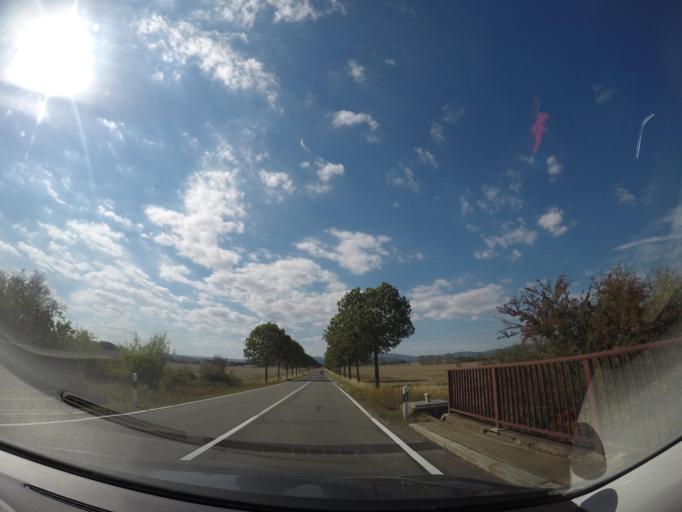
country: DE
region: Saxony-Anhalt
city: Langeln
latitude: 51.9237
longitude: 10.8005
